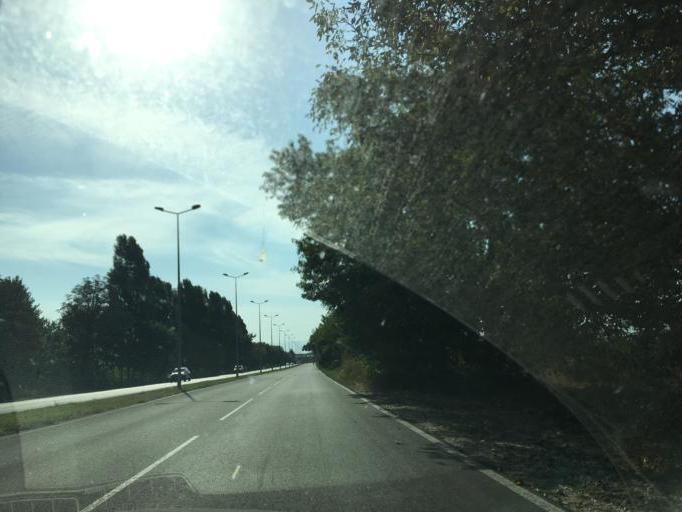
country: BG
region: Pazardzhik
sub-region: Obshtina Pazardzhik
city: Pazardzhik
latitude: 42.2167
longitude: 24.3175
